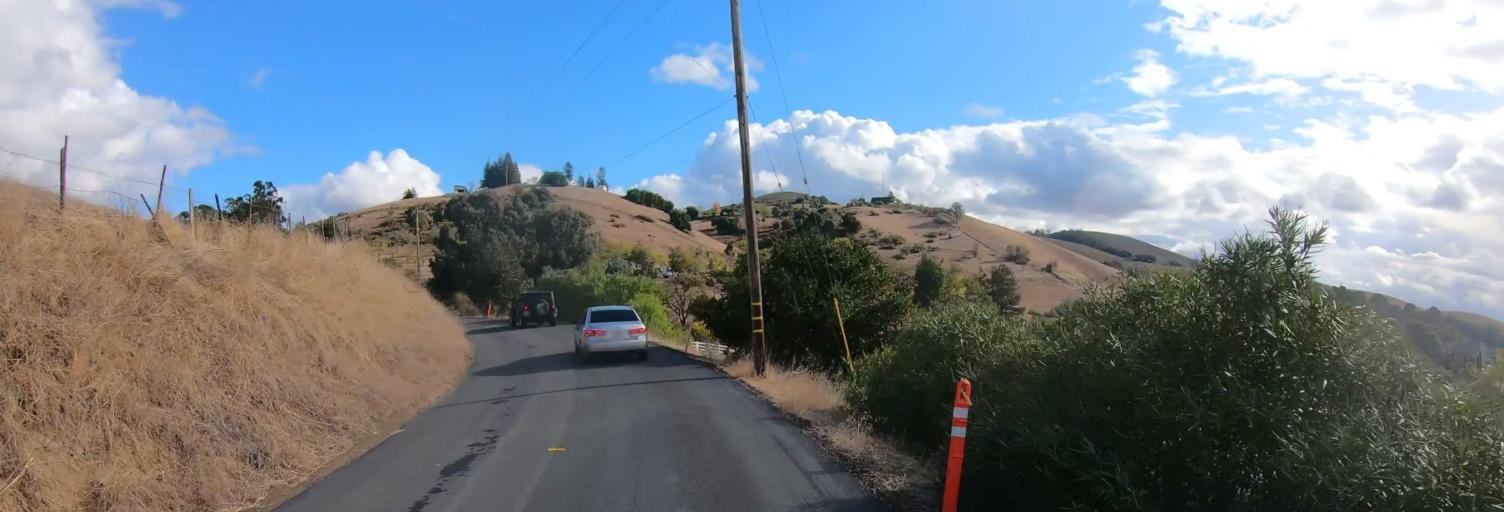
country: US
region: California
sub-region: Santa Clara County
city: East Foothills
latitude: 37.3635
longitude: -121.7606
